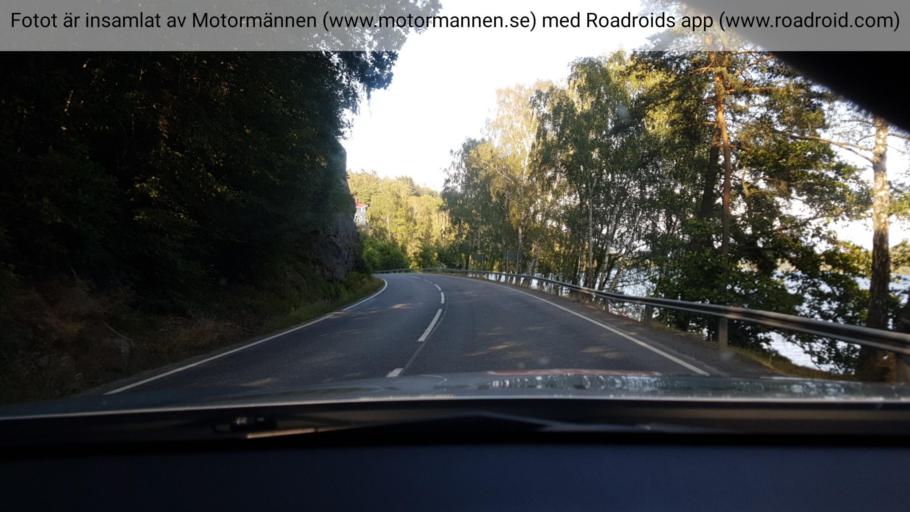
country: SE
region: Vaestra Goetaland
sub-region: Harryda Kommun
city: Molnlycke
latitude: 57.6756
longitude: 12.1572
